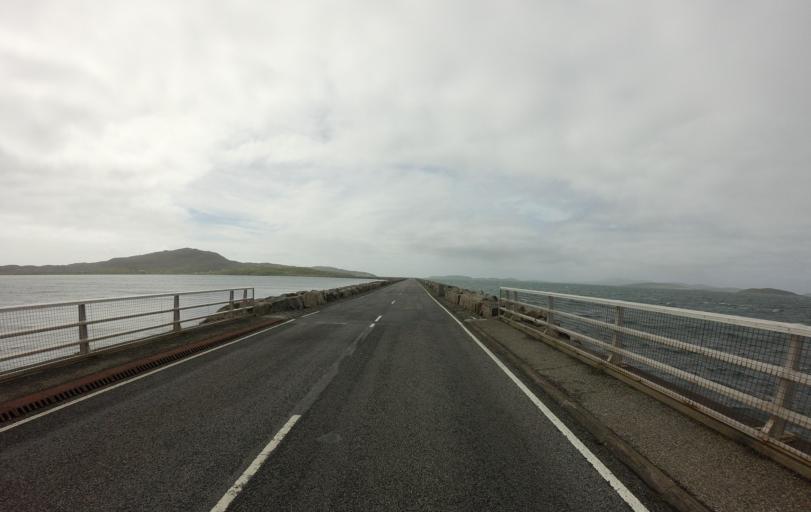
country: GB
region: Scotland
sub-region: Eilean Siar
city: Isle of South Uist
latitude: 57.0985
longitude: -7.3176
